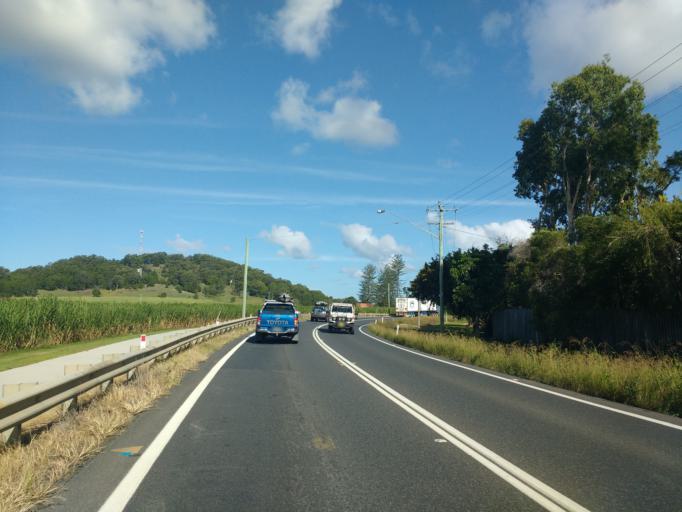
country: AU
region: New South Wales
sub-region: Richmond Valley
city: Evans Head
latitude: -29.0064
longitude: 153.4364
